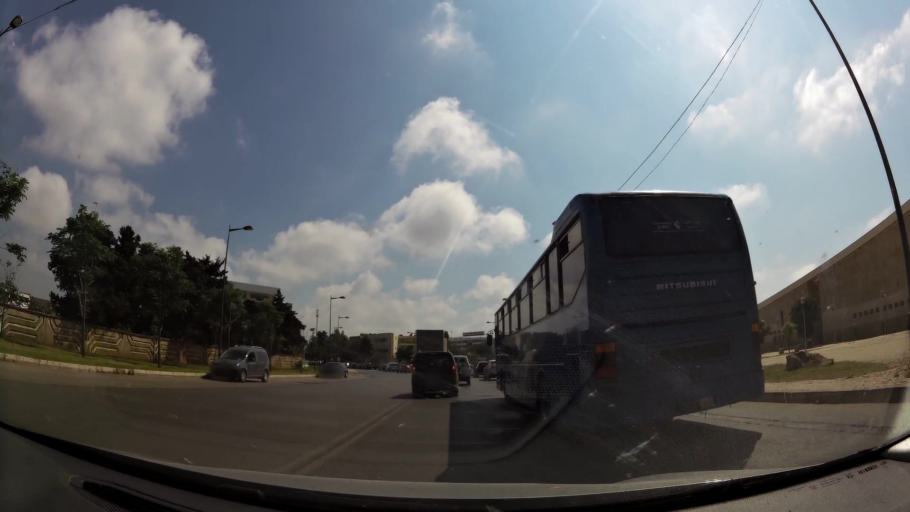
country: MA
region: Rabat-Sale-Zemmour-Zaer
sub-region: Rabat
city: Rabat
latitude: 33.9752
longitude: -6.8703
